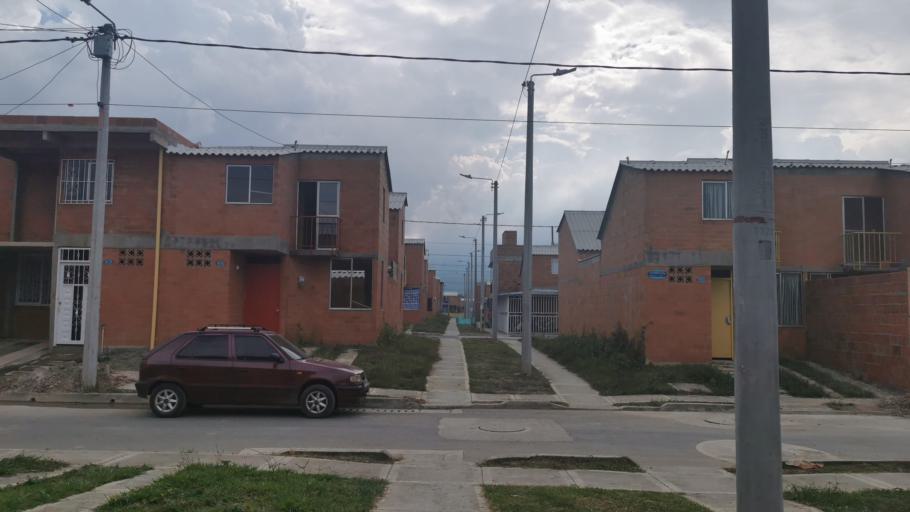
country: CO
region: Valle del Cauca
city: Jamundi
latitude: 3.2343
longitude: -76.5252
